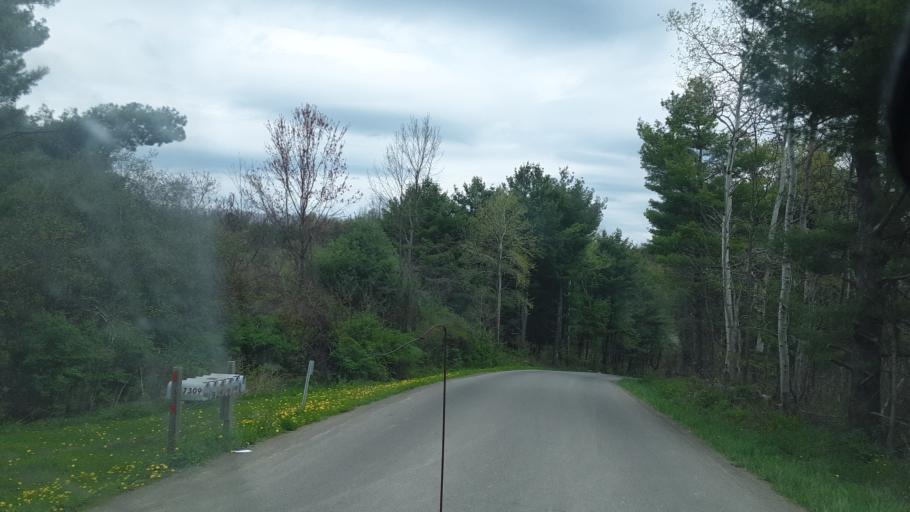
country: US
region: New York
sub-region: Steuben County
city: Addison
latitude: 42.0955
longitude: -77.2751
